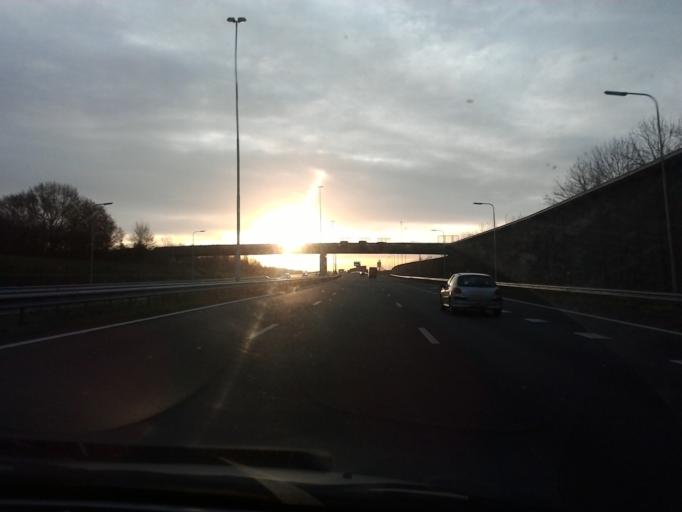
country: NL
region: North Brabant
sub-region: Gemeente Best
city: Best
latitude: 51.5106
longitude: 5.4067
